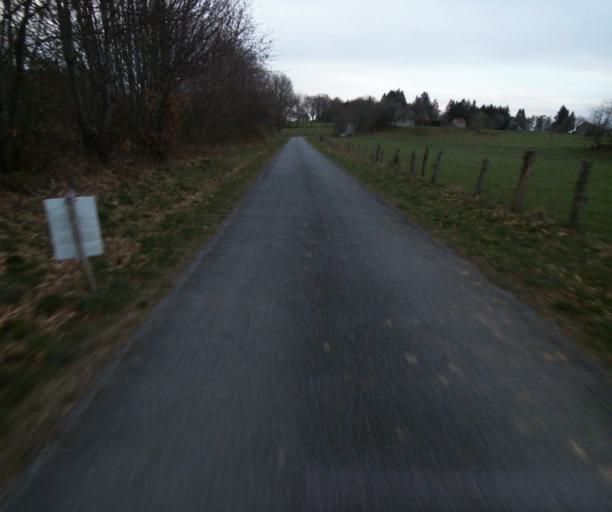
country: FR
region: Limousin
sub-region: Departement de la Correze
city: Correze
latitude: 45.4416
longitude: 1.8378
